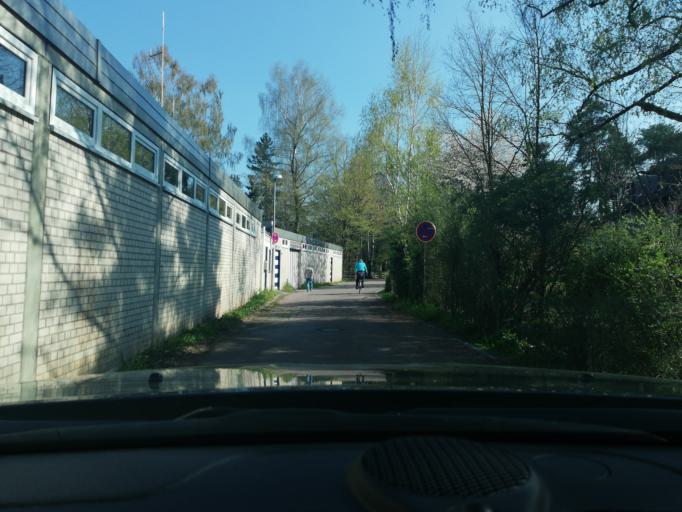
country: DE
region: Bavaria
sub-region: Regierungsbezirk Mittelfranken
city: Hessdorf
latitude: 49.6290
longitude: 10.9526
